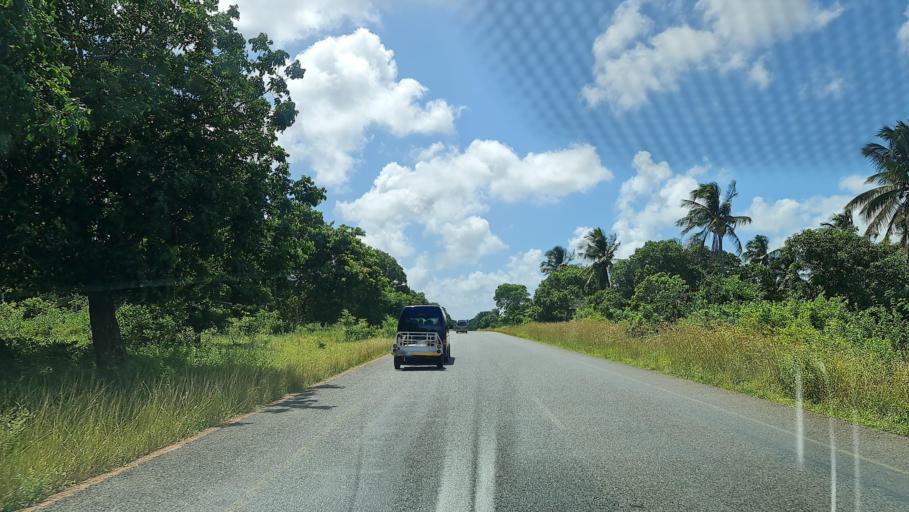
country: MZ
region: Inhambane
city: Maxixe
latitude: -24.5406
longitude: 34.9237
